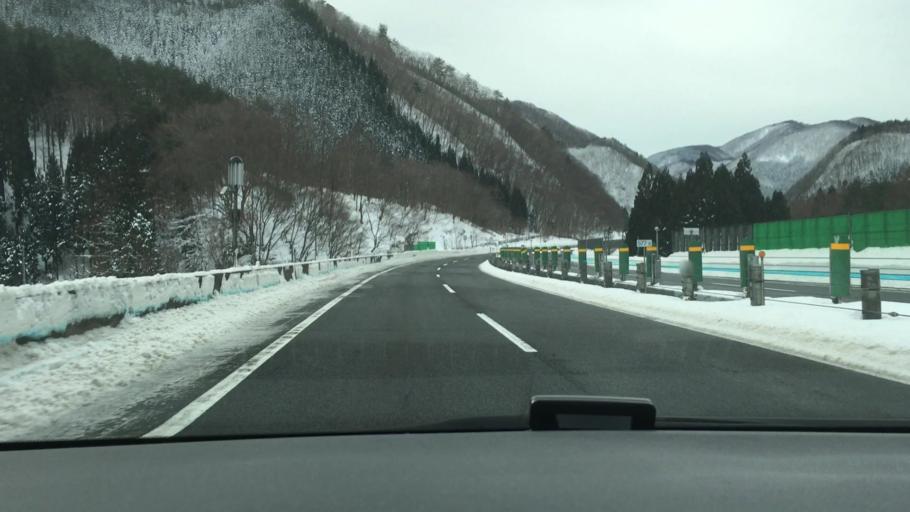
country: JP
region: Akita
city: Hanawa
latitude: 40.1278
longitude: 140.9117
